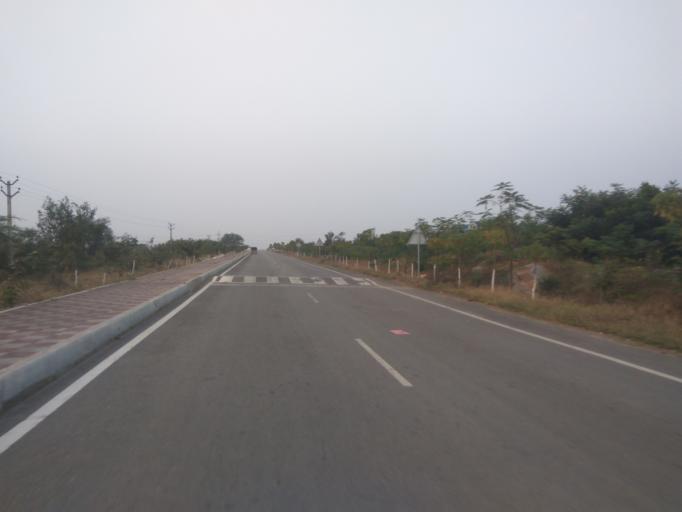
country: IN
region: Telangana
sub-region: Rangareddi
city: Secunderabad
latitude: 17.5426
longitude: 78.6307
